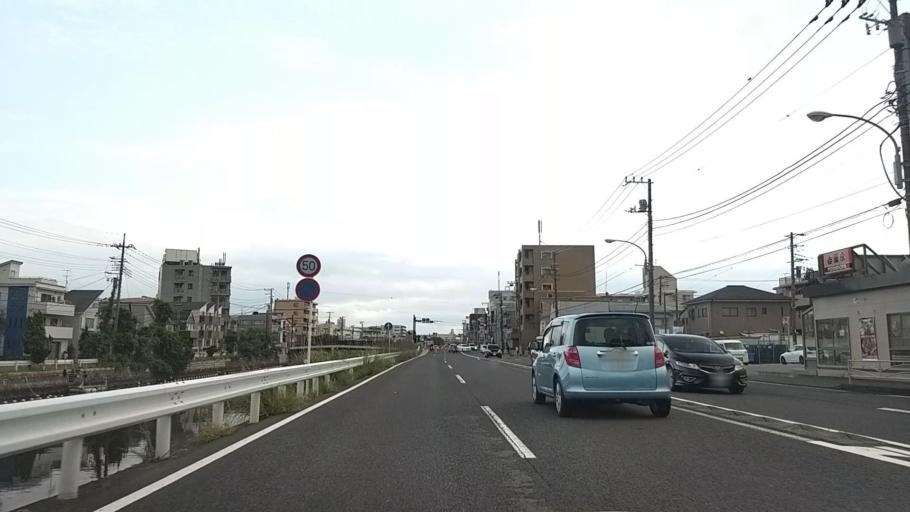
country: JP
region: Kanagawa
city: Yokohama
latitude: 35.4239
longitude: 139.6241
